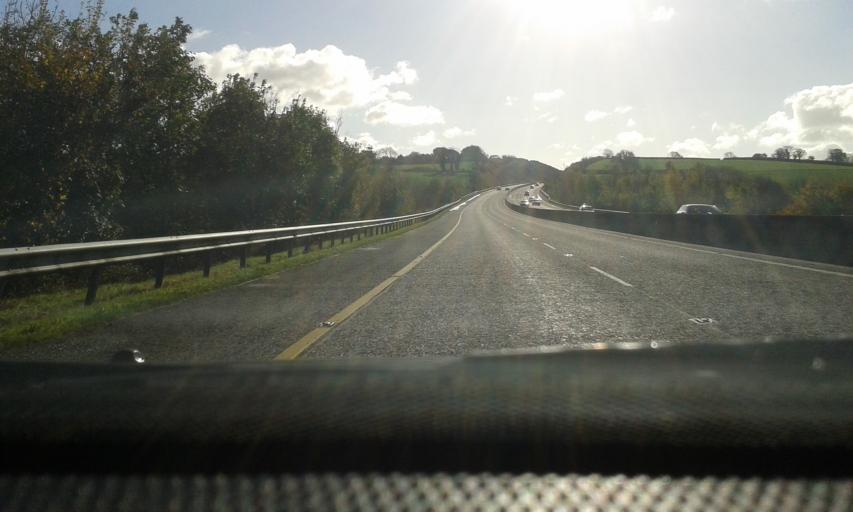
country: IE
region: Munster
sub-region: County Cork
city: Rathcormac
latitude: 52.0640
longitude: -8.3046
